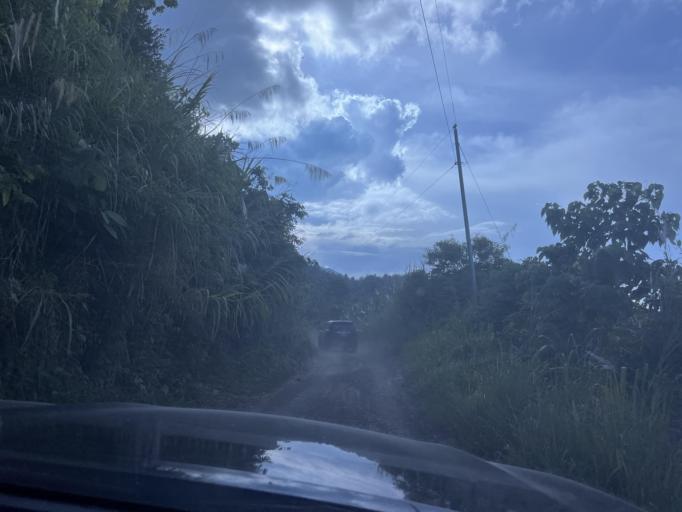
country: PH
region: Davao
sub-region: Province of Davao del Sur
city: Pung-Pang
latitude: 6.4794
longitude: 125.4484
